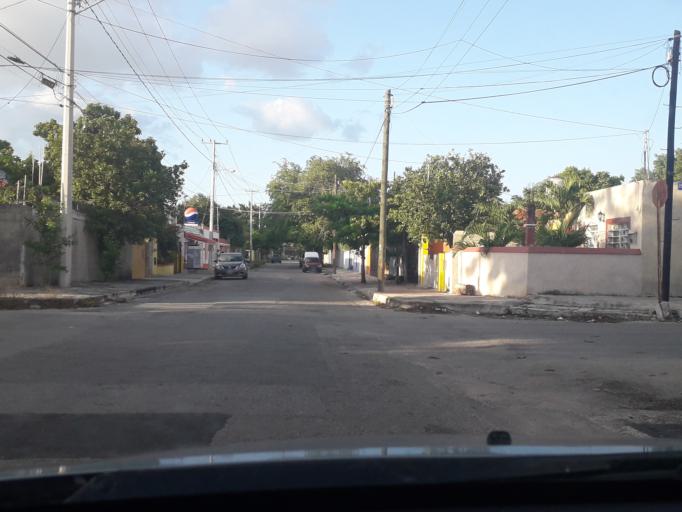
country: MX
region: Yucatan
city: Merida
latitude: 20.9763
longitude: -89.6481
